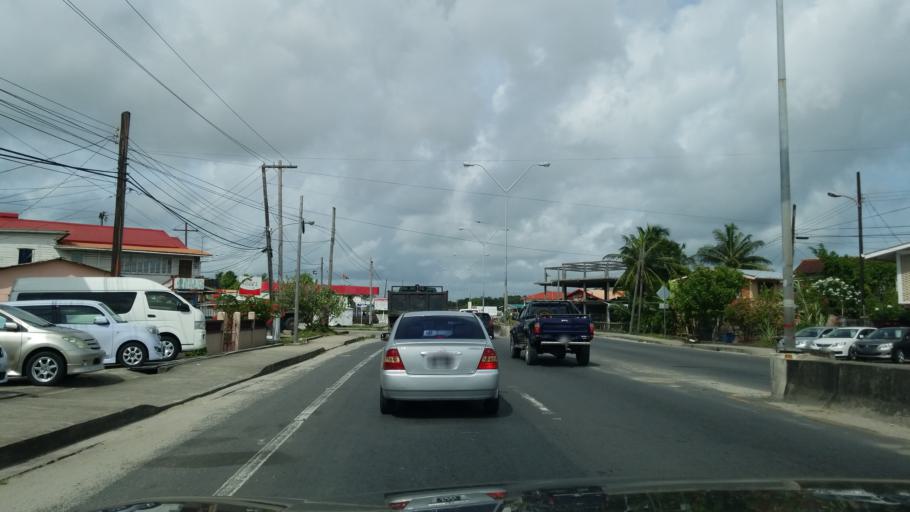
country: GY
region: Demerara-Mahaica
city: Georgetown
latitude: 6.7724
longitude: -58.1738
